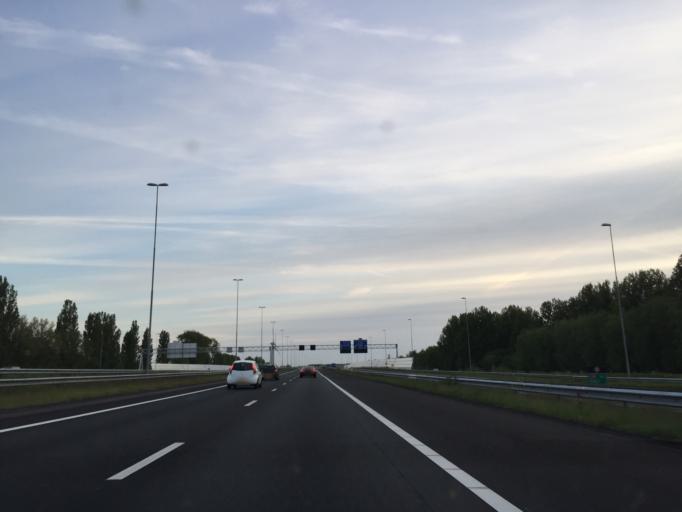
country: NL
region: South Holland
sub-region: Gemeente Leiden
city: Leiden
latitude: 52.1352
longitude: 4.5020
